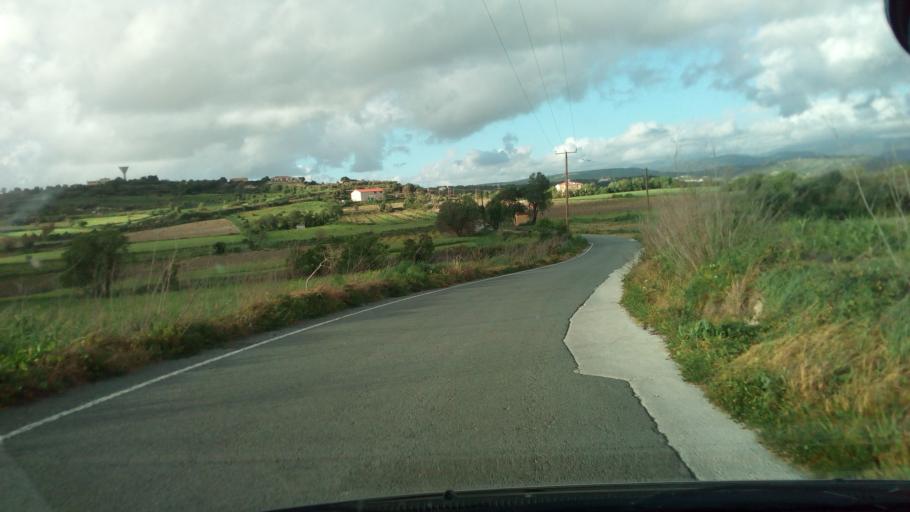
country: CY
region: Pafos
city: Mesogi
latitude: 34.8695
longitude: 32.5042
